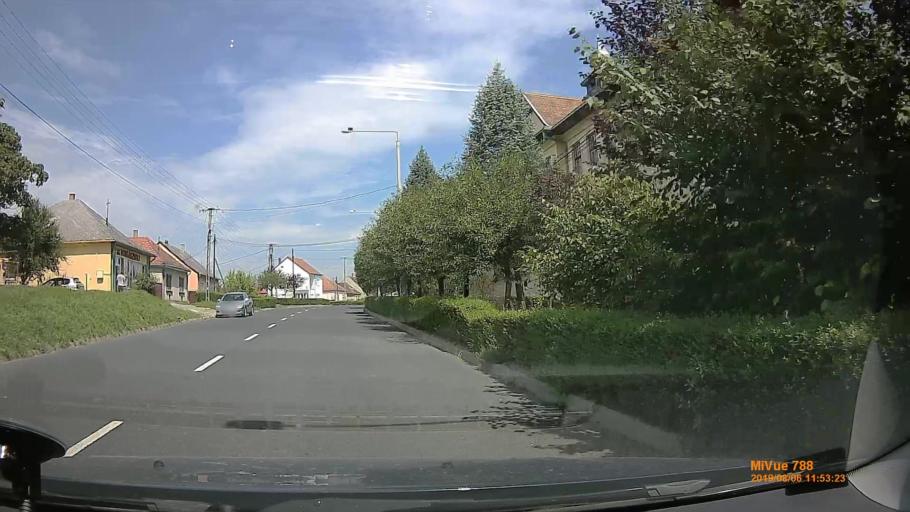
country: HU
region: Zala
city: Letenye
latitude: 46.4285
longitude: 16.7221
